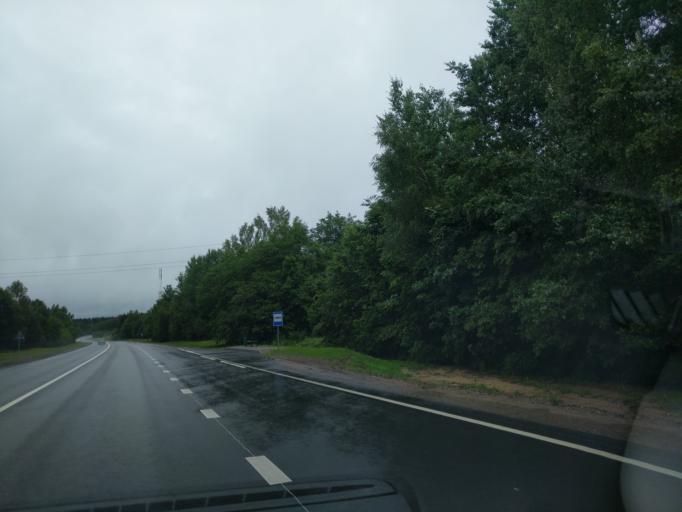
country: BY
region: Minsk
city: Syomkava
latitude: 54.1618
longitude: 27.5019
